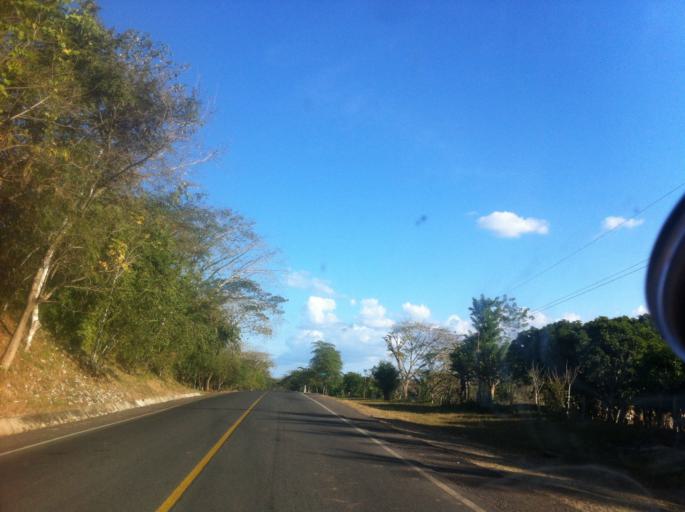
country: NI
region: Rio San Juan
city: Morrito
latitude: 11.7282
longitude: -84.9706
